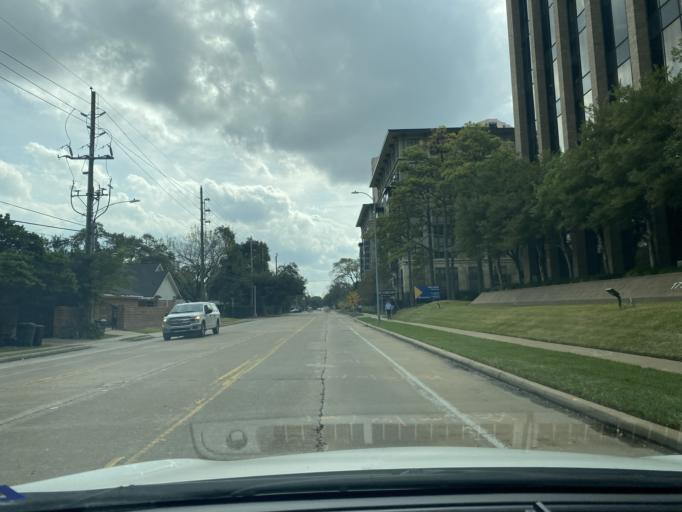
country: US
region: Texas
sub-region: Harris County
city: Hunters Creek Village
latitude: 29.7477
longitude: -95.4709
